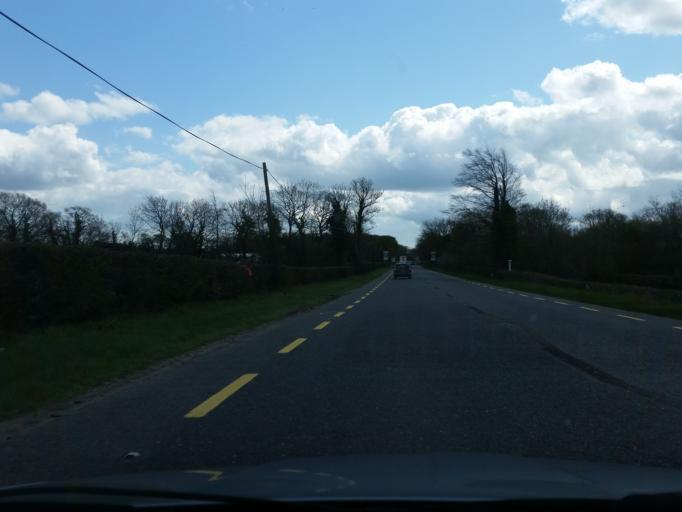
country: IE
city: Kentstown
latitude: 53.6448
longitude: -6.5057
